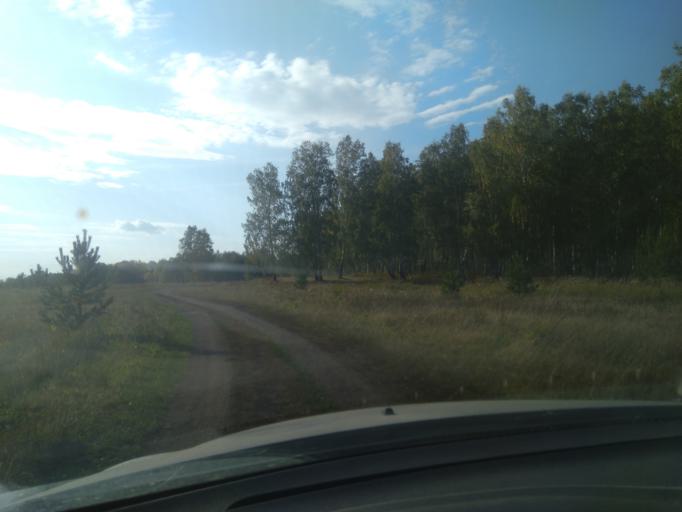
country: RU
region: Sverdlovsk
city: Pokrovskoye
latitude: 56.4296
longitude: 61.6013
